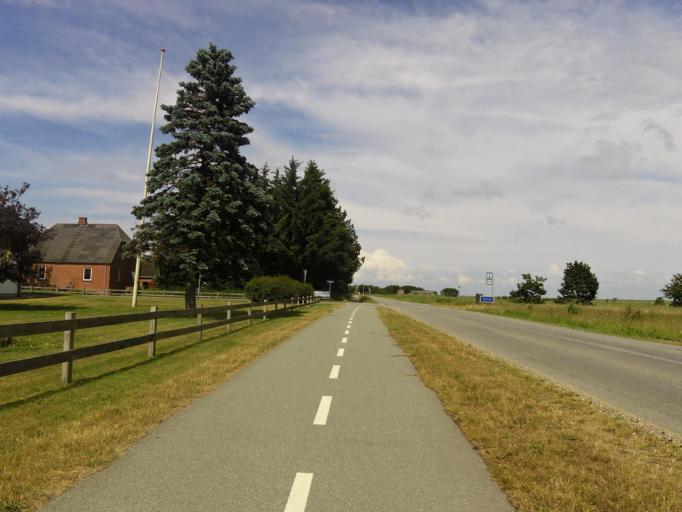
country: DE
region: Schleswig-Holstein
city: List
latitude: 55.1619
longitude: 8.5530
